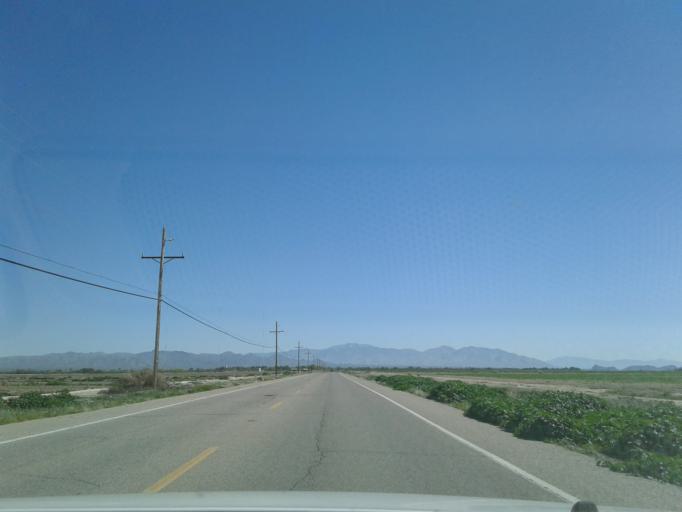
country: US
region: Arizona
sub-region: Pima County
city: Avra Valley
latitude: 32.4512
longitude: -111.2980
